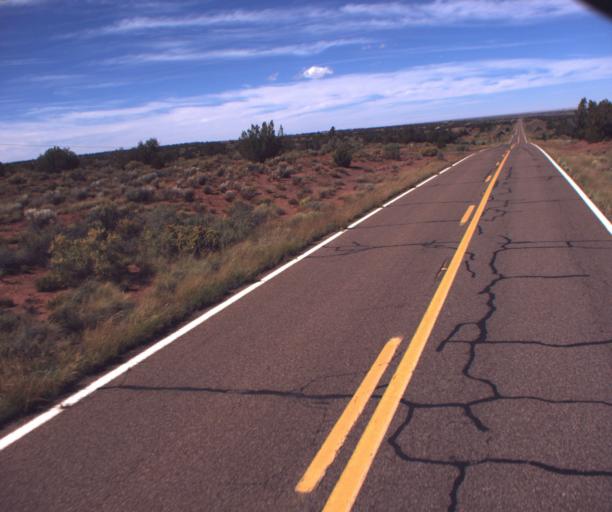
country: US
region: Arizona
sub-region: Apache County
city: Saint Johns
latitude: 34.5933
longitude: -109.6479
